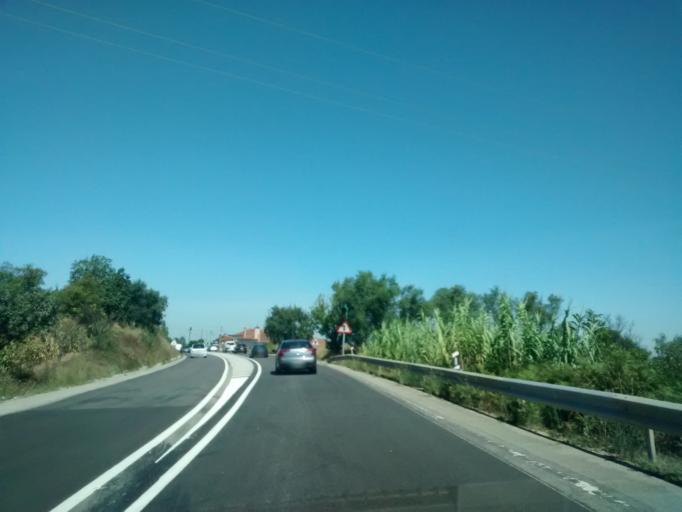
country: PT
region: Aveiro
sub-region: Oliveira do Bairro
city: Oia
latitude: 40.5470
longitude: -8.5364
